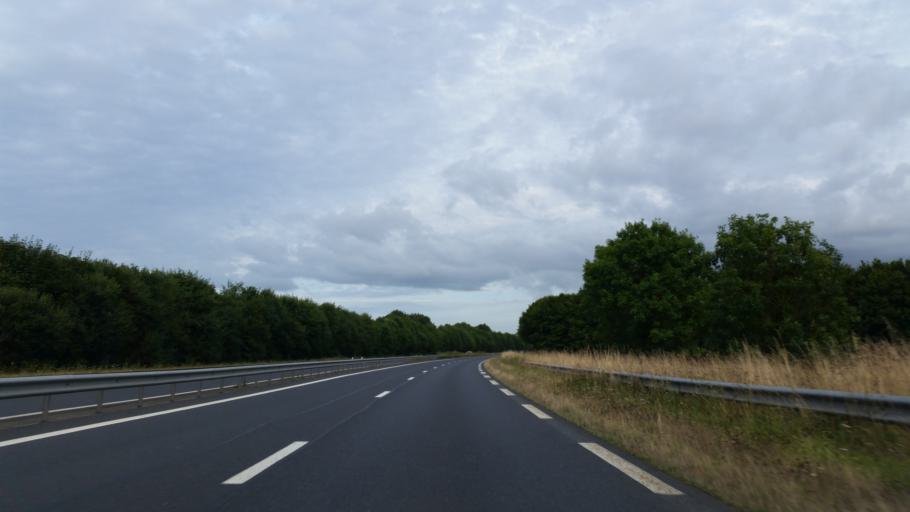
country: FR
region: Lower Normandy
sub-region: Departement du Calvados
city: Grandcamp-Maisy
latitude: 49.3443
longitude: -0.9634
